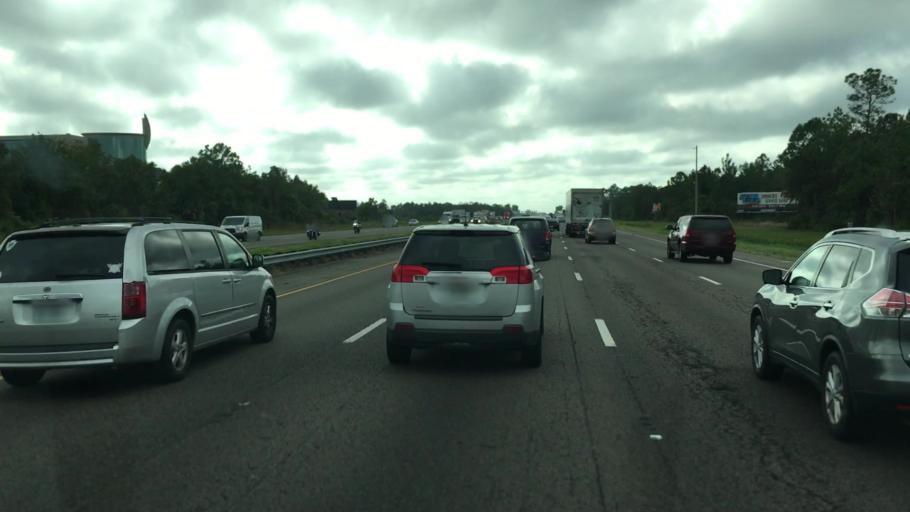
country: US
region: Florida
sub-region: Volusia County
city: Ormond Beach
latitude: 29.2473
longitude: -81.1128
